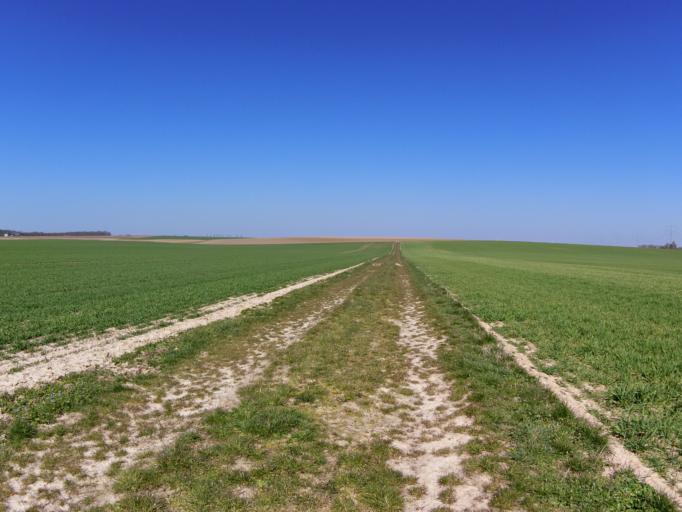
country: DE
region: Bavaria
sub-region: Regierungsbezirk Unterfranken
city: Oberpleichfeld
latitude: 49.8379
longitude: 10.0863
